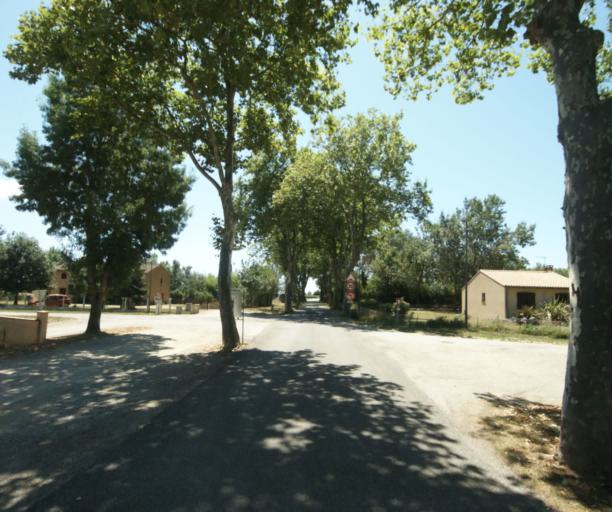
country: FR
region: Midi-Pyrenees
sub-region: Departement de la Haute-Garonne
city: Saint-Felix-Lauragais
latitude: 43.4619
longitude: 1.9287
